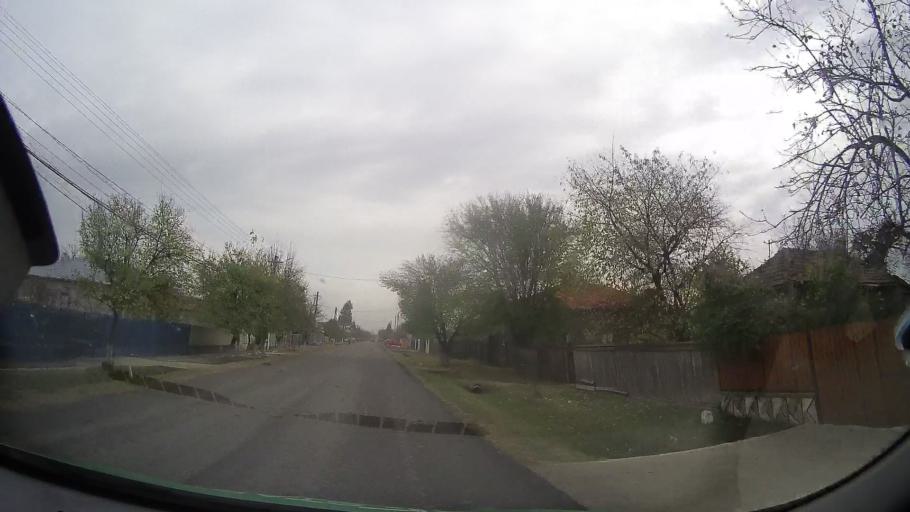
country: RO
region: Prahova
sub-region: Comuna Dumbrava
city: Dumbrava
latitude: 44.8718
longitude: 26.1918
